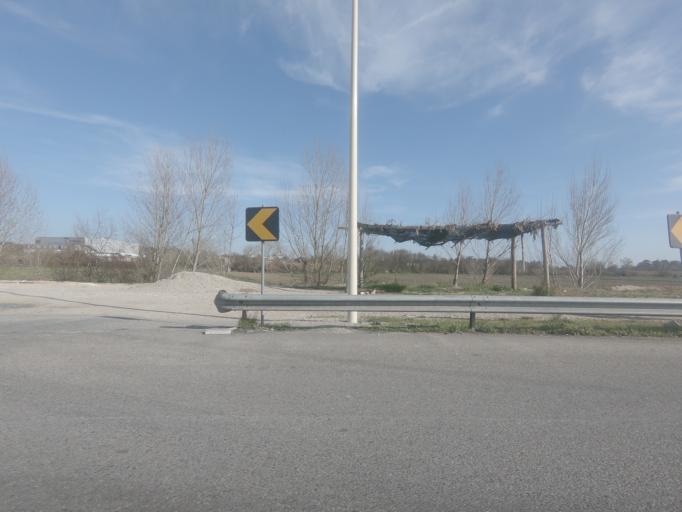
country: PT
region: Santarem
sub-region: Torres Novas
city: Torres Novas
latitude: 39.4641
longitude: -8.5294
